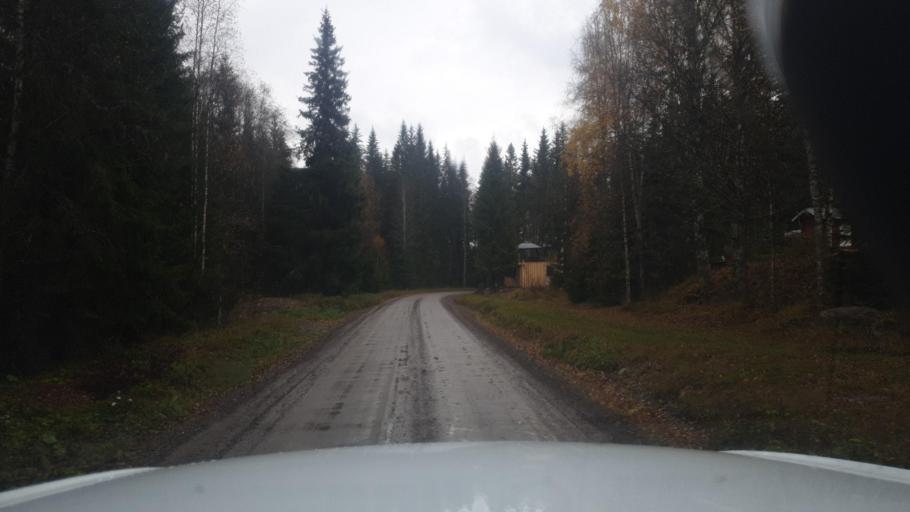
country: SE
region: Vaermland
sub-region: Eda Kommun
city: Charlottenberg
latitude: 60.0355
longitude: 12.5943
